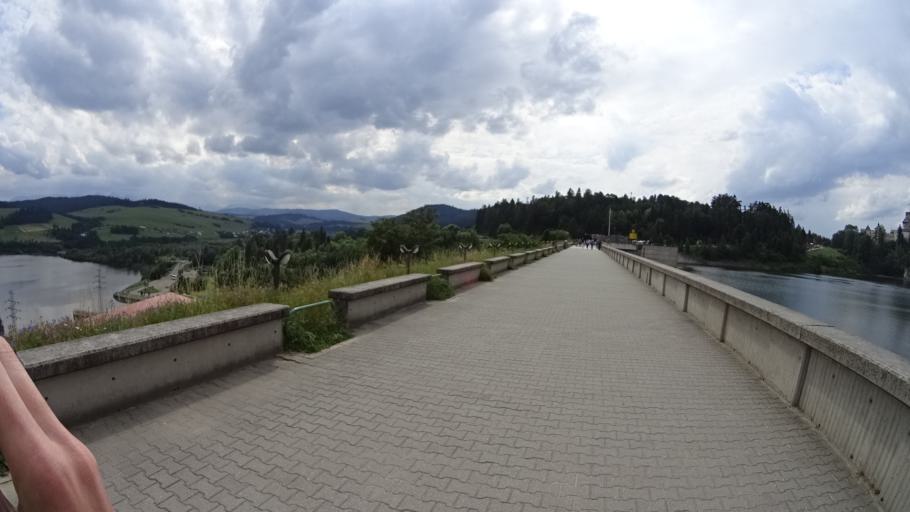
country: PL
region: Lesser Poland Voivodeship
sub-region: Powiat nowotarski
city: Niedzica
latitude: 49.4197
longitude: 20.3243
